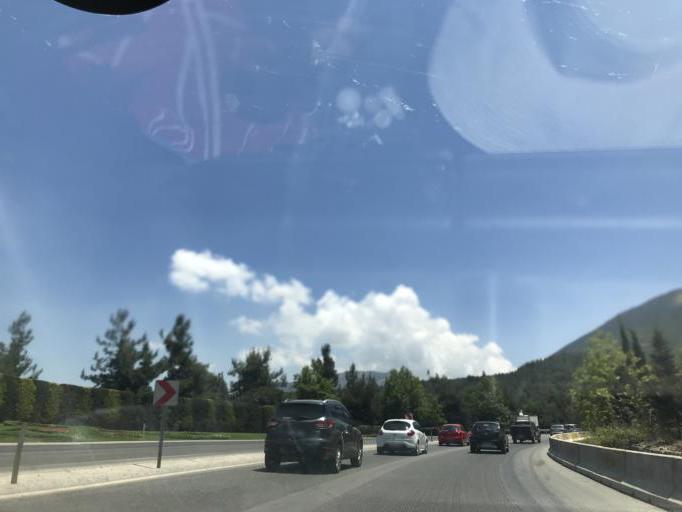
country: TR
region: Denizli
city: Denizli
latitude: 37.7309
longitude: 29.1640
